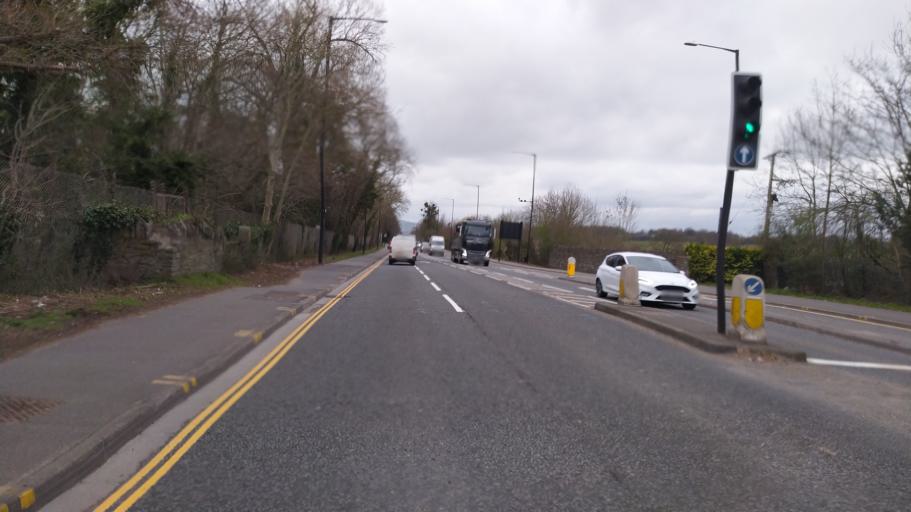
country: GB
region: England
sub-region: Bath and North East Somerset
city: Whitchurch
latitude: 51.4287
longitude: -2.5354
